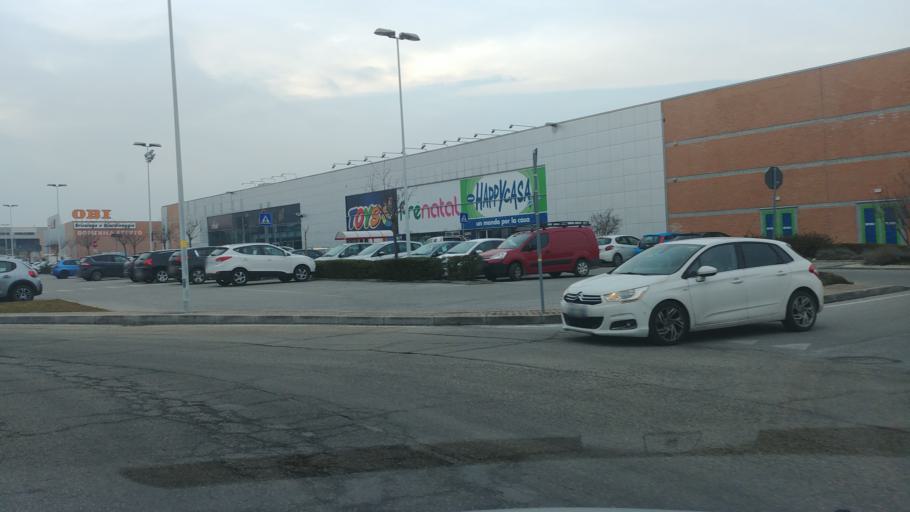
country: IT
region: Piedmont
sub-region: Provincia di Cuneo
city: Cuneo
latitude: 44.4222
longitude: 7.5523
